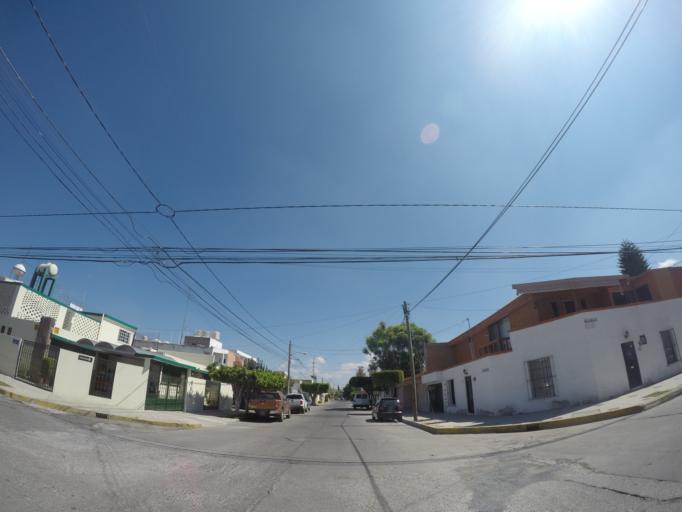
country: MX
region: San Luis Potosi
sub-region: San Luis Potosi
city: San Luis Potosi
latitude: 22.1429
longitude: -101.0084
